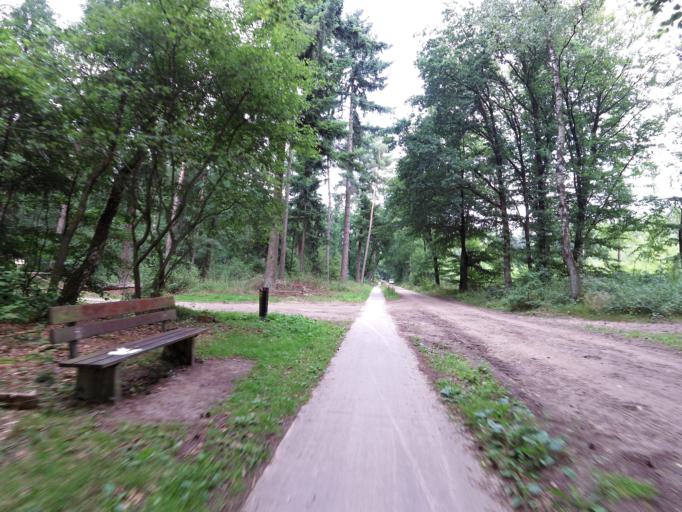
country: NL
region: Gelderland
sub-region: Gemeente Montferland
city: s-Heerenberg
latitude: 51.8977
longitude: 6.2394
